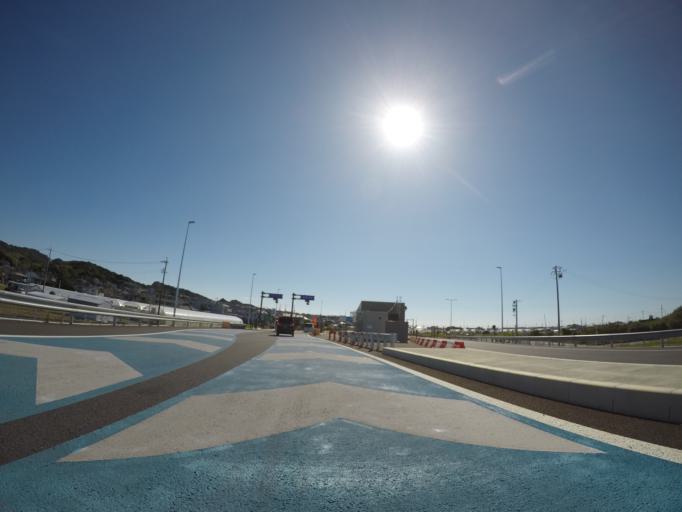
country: JP
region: Shizuoka
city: Shizuoka-shi
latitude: 34.9603
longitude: 138.4238
